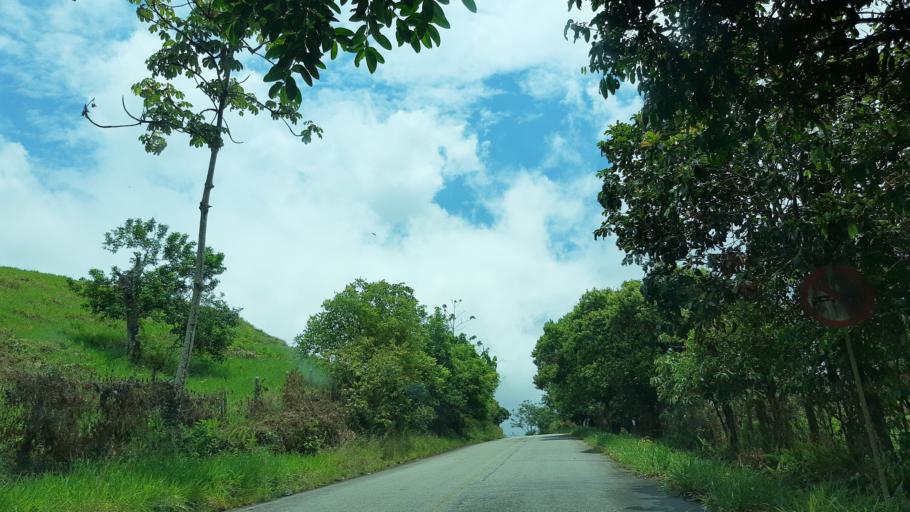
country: CO
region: Casanare
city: Sabanalarga
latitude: 4.8243
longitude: -73.0528
